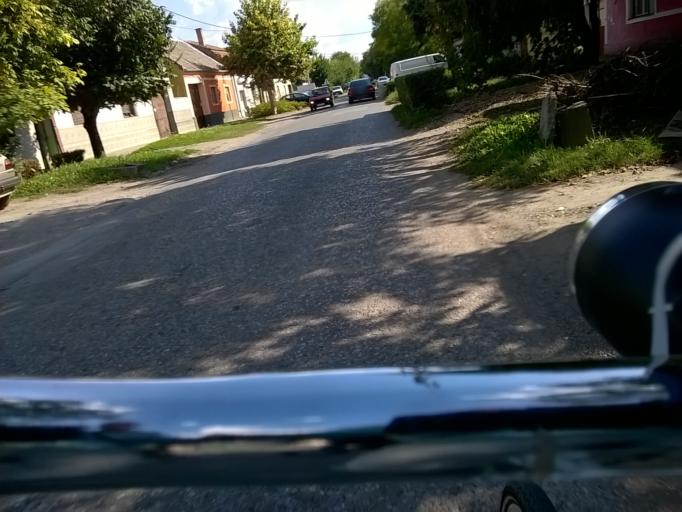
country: RS
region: Autonomna Pokrajina Vojvodina
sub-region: Juznobanatski Okrug
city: Pancevo
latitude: 44.8779
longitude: 20.6433
